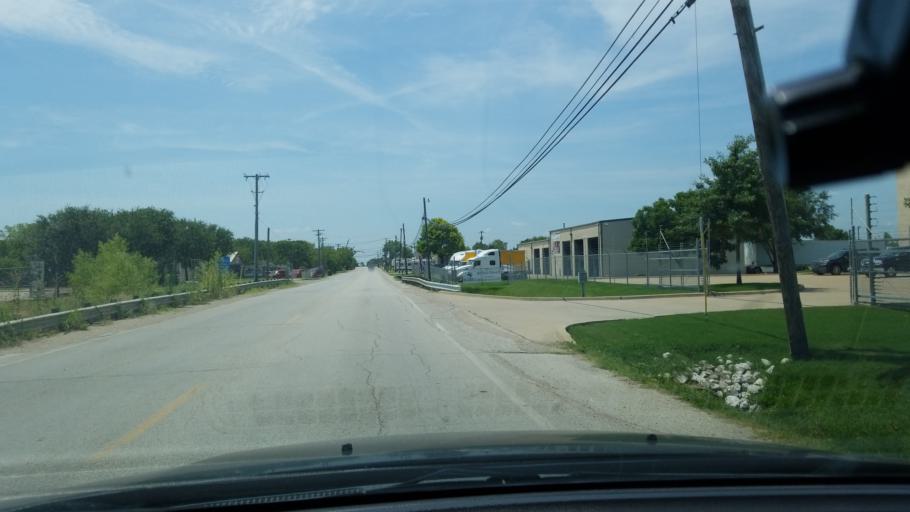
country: US
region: Texas
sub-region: Dallas County
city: Balch Springs
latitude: 32.7462
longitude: -96.6313
